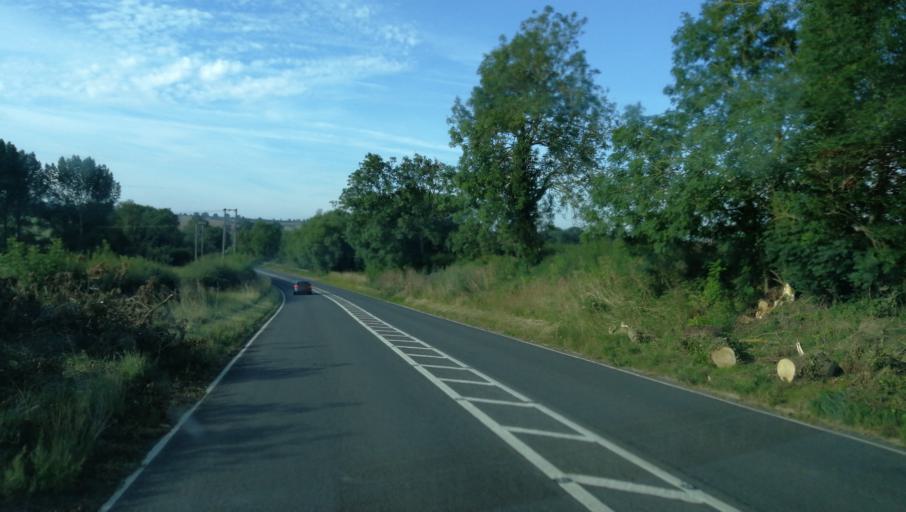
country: GB
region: England
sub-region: Oxfordshire
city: Deddington
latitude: 51.9704
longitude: -1.3193
